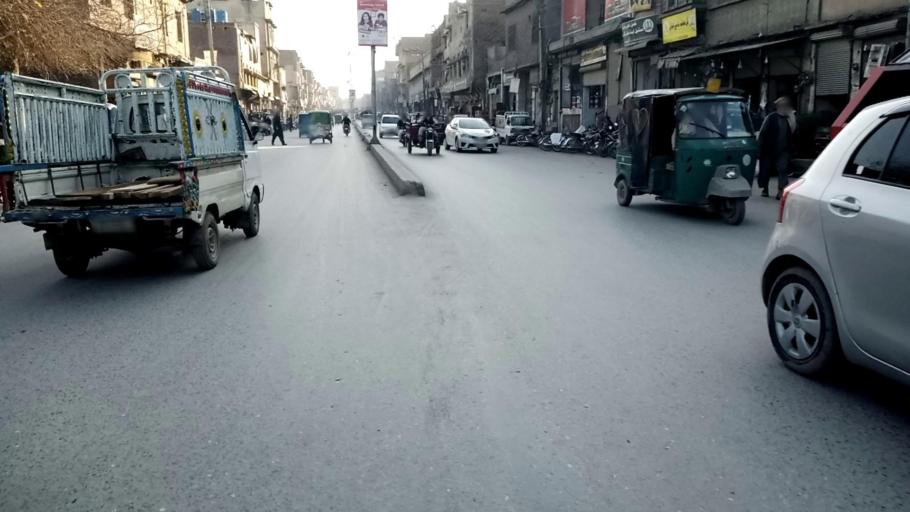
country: PK
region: Khyber Pakhtunkhwa
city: Peshawar
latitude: 34.0103
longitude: 71.5853
